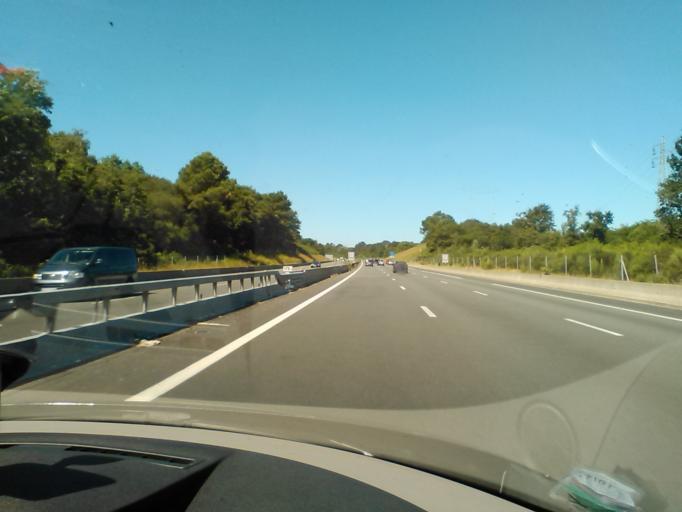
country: FR
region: Aquitaine
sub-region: Departement des Pyrenees-Atlantiques
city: Anglet
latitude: 43.4615
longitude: -1.5065
